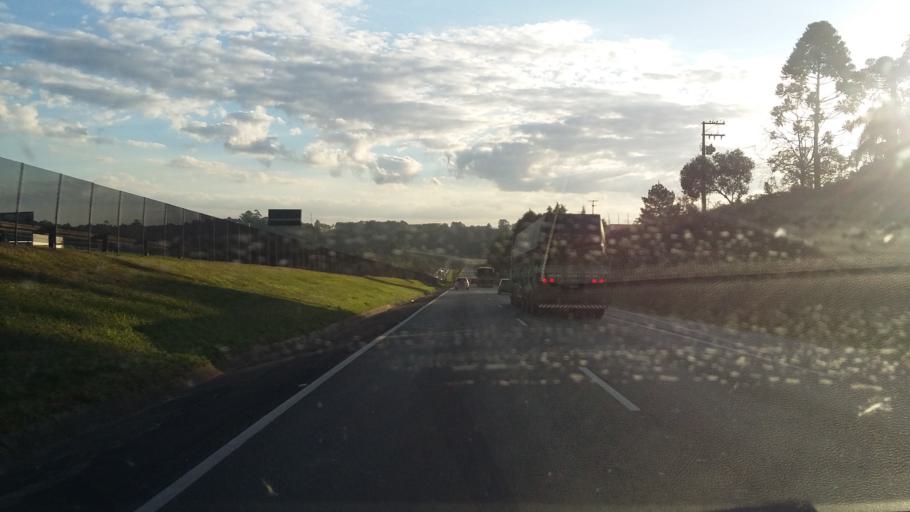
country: BR
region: Parana
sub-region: Campo Largo
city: Campo Largo
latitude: -25.4430
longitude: -49.4555
